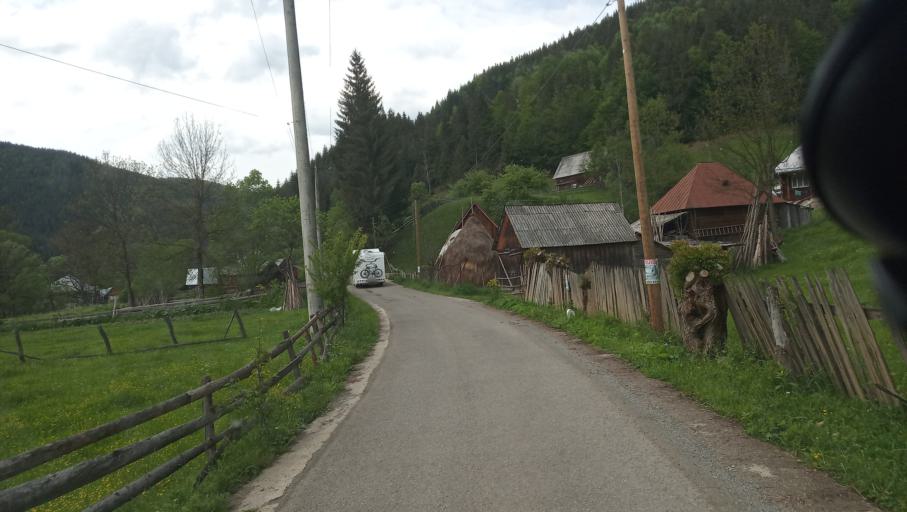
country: RO
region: Alba
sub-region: Comuna Garda de Sus
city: Garda de Sus
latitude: 46.4784
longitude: 22.8084
